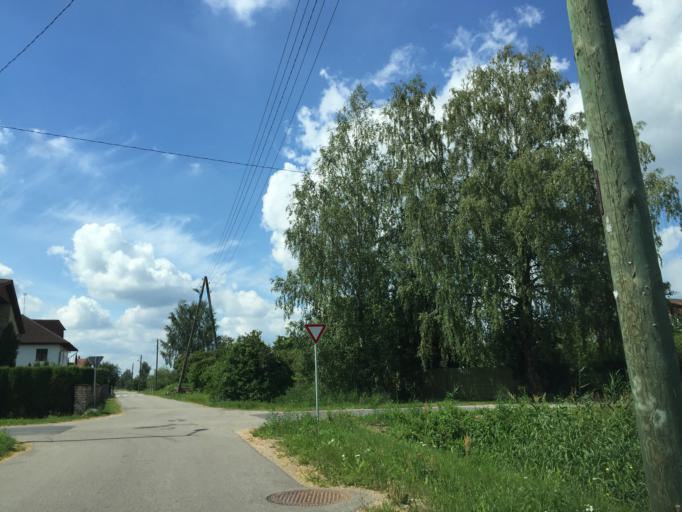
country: LV
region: Olaine
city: Olaine
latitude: 56.8041
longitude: 23.9844
